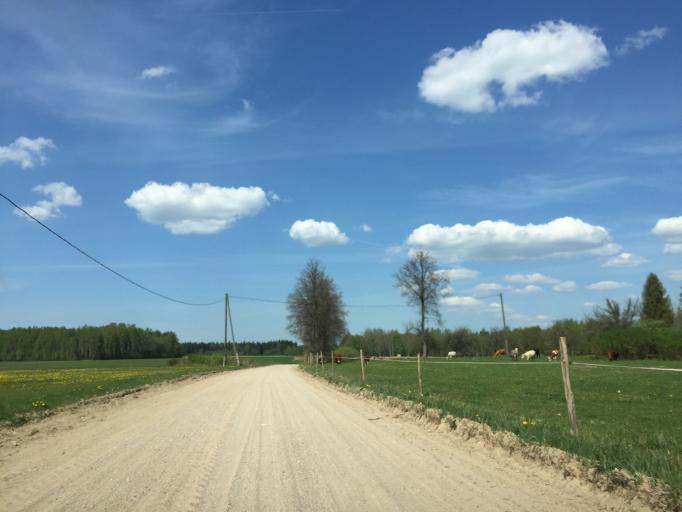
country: LV
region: Limbazu Rajons
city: Limbazi
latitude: 57.3561
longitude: 24.6448
